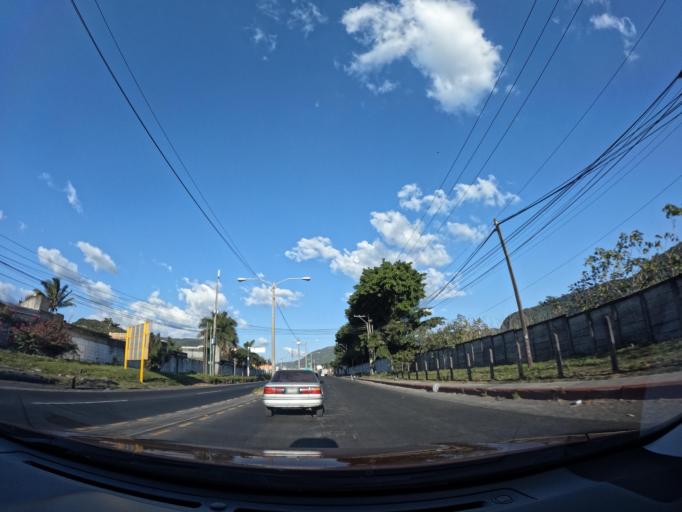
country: GT
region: Escuintla
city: Palin
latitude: 14.4089
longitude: -90.6853
